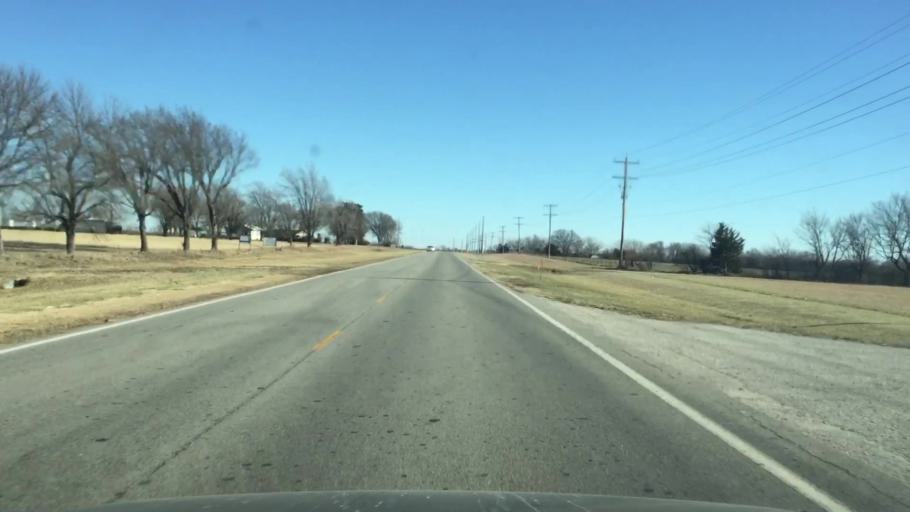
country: US
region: Kansas
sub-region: Allen County
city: Humboldt
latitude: 37.8201
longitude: -95.4258
